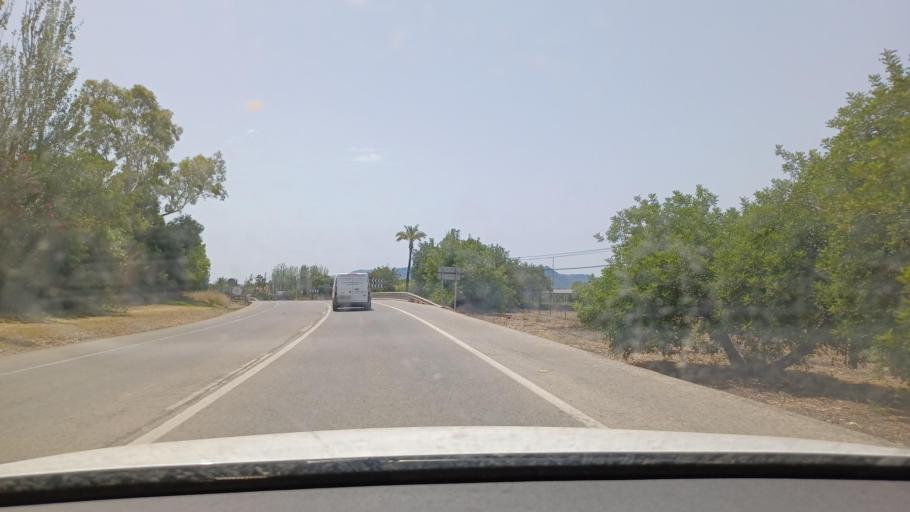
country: ES
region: Catalonia
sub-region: Provincia de Tarragona
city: Vilanova d'Escornalbou
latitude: 41.0369
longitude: 0.9720
